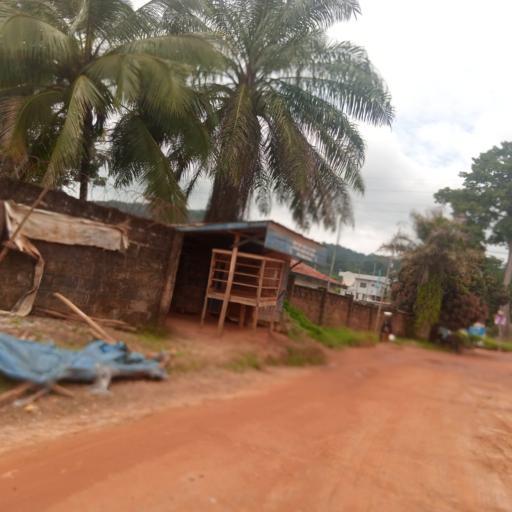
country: SL
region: Eastern Province
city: Kenema
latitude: 7.8773
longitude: -11.1944
